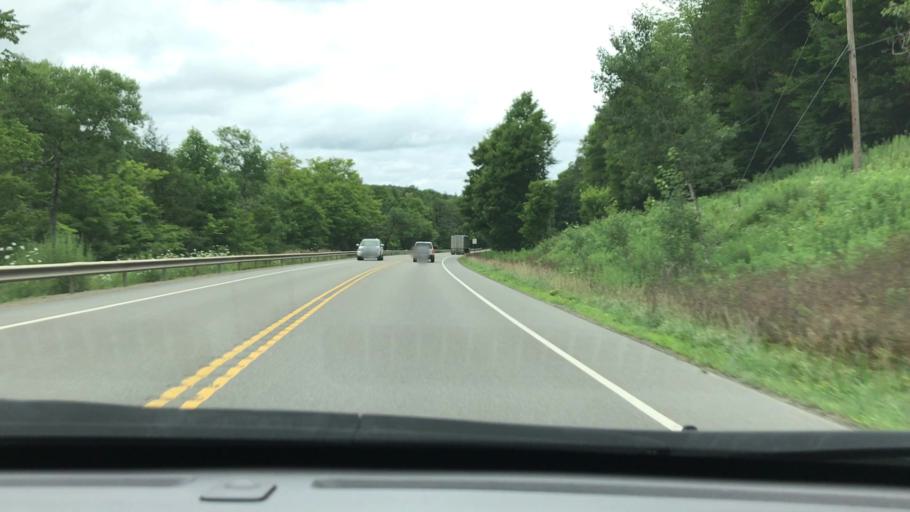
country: US
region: Pennsylvania
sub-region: McKean County
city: Kane
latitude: 41.6764
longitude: -78.6849
